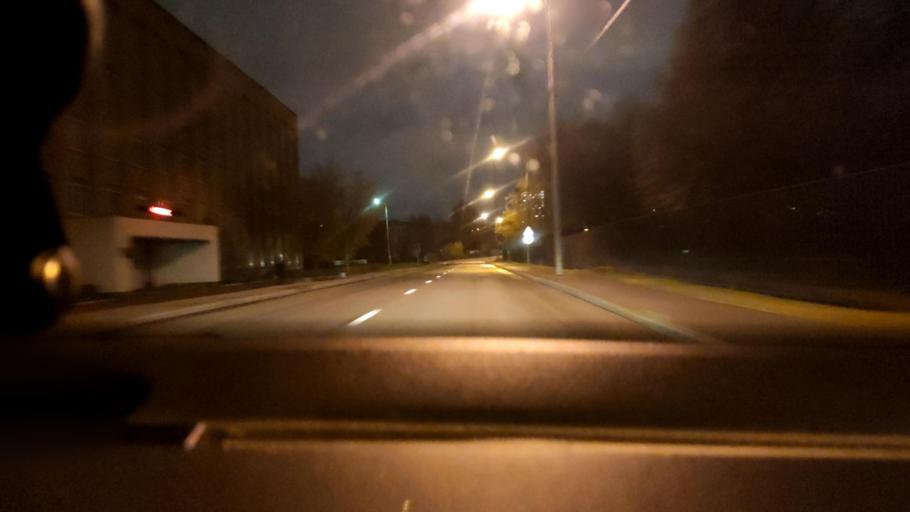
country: RU
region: Moscow
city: Likhobory
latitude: 55.8317
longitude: 37.5570
